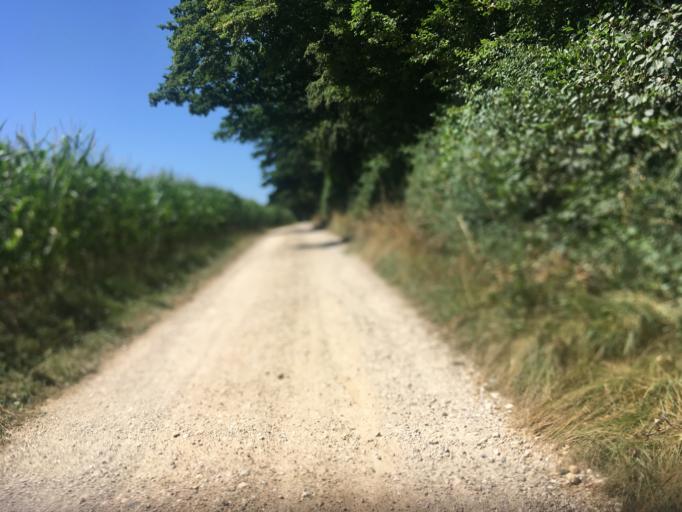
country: CH
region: Solothurn
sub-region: Bezirk Bucheggberg
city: Messen
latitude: 47.0745
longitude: 7.4447
